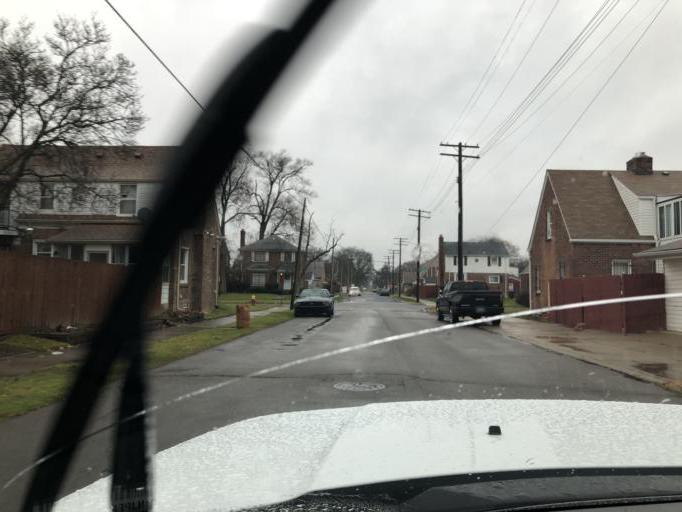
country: US
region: Michigan
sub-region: Oakland County
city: Oak Park
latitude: 42.4102
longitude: -83.2147
